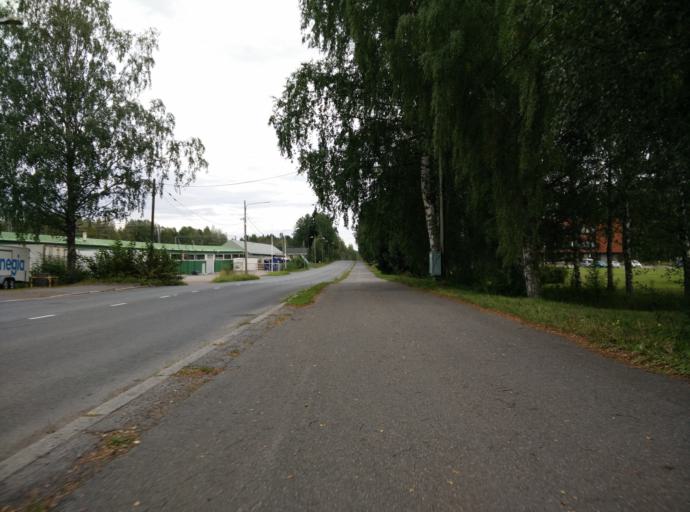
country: FI
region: Haeme
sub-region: Haemeenlinna
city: Haemeenlinna
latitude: 60.9918
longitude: 24.4921
